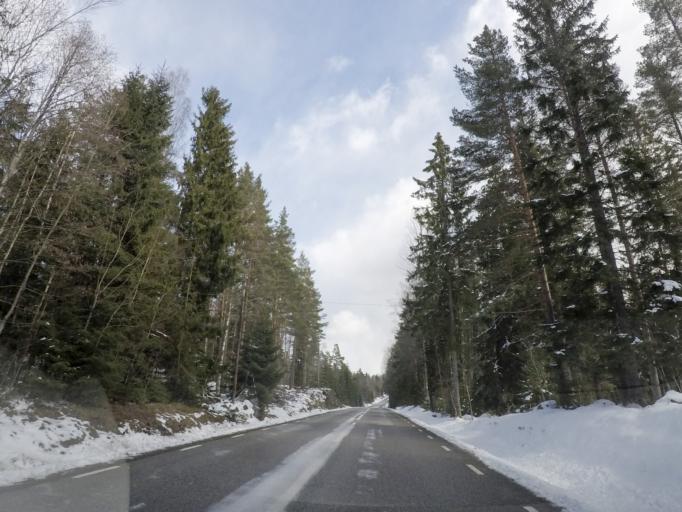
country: SE
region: OErebro
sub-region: Lindesbergs Kommun
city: Stora
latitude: 59.8956
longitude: 15.2345
